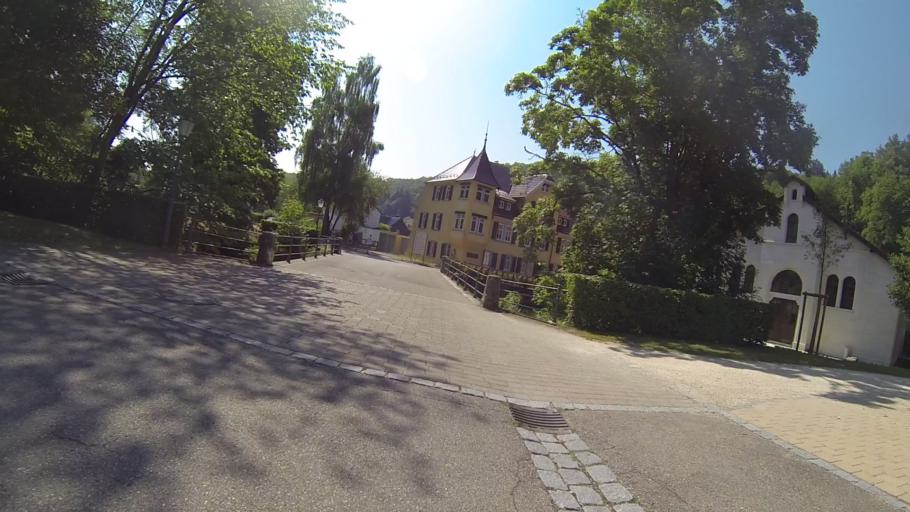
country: DE
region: Baden-Wuerttemberg
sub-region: Regierungsbezirk Stuttgart
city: Konigsbronn
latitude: 48.7383
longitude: 10.1136
